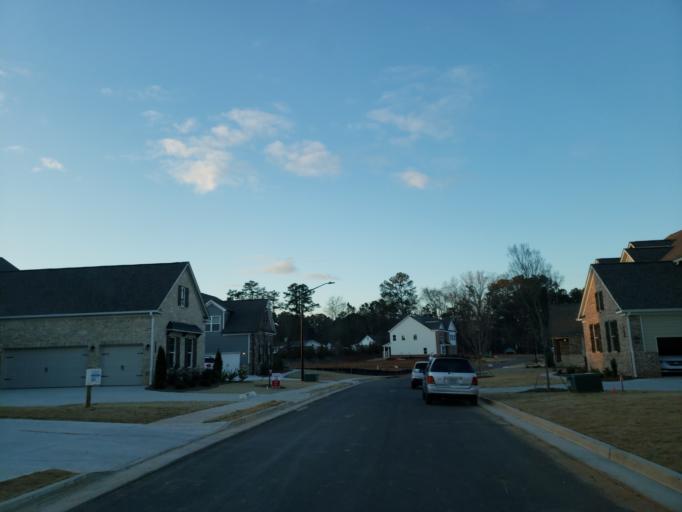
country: US
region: Georgia
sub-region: Cobb County
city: Acworth
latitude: 33.9755
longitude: -84.7171
